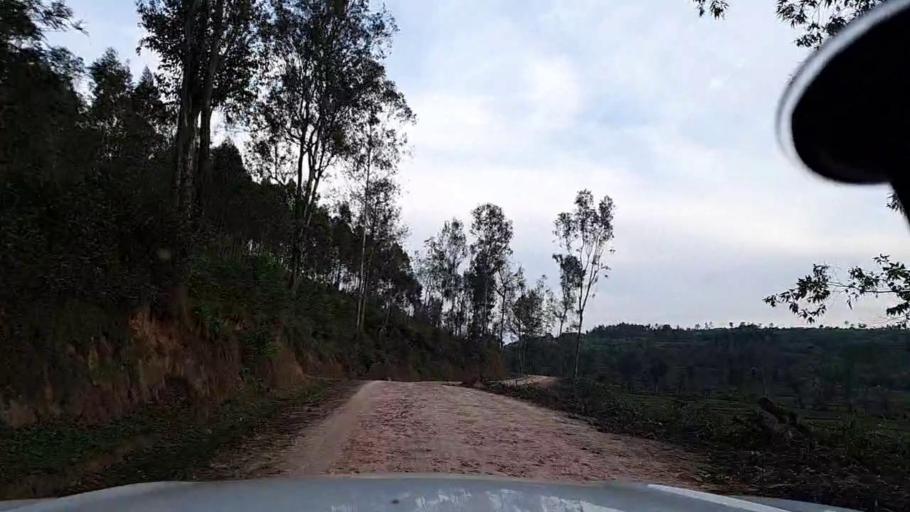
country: RW
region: Southern Province
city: Gitarama
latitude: -2.2095
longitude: 29.6174
